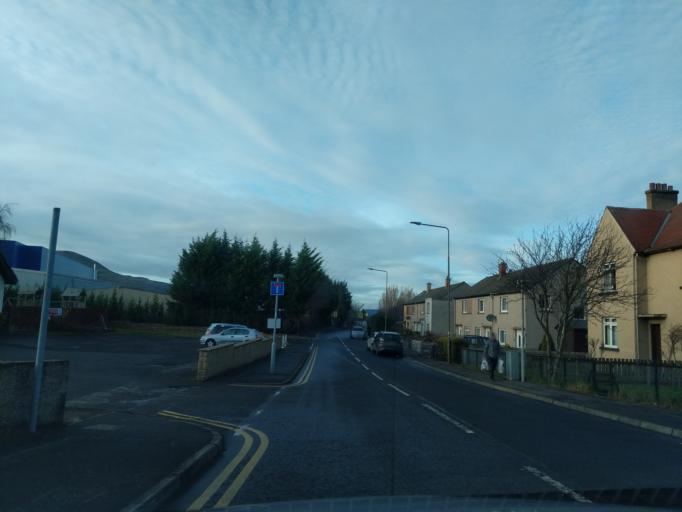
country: GB
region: Scotland
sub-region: Midlothian
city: Loanhead
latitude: 55.8771
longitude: -3.1643
